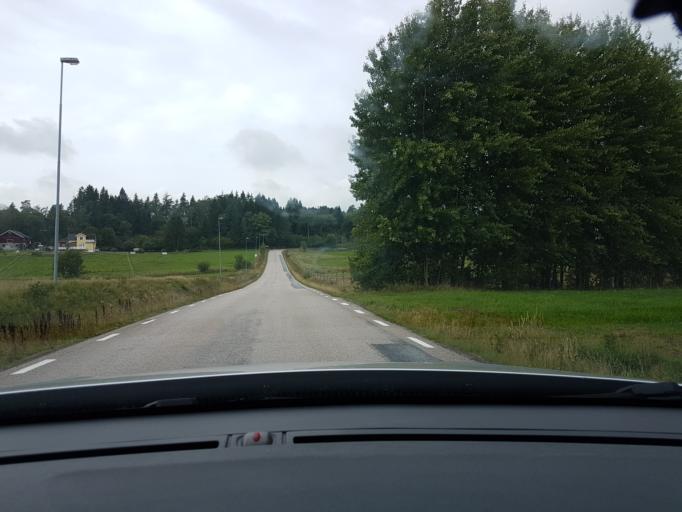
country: SE
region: Vaestra Goetaland
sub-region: Ale Kommun
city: Alvangen
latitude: 57.9176
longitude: 12.1376
